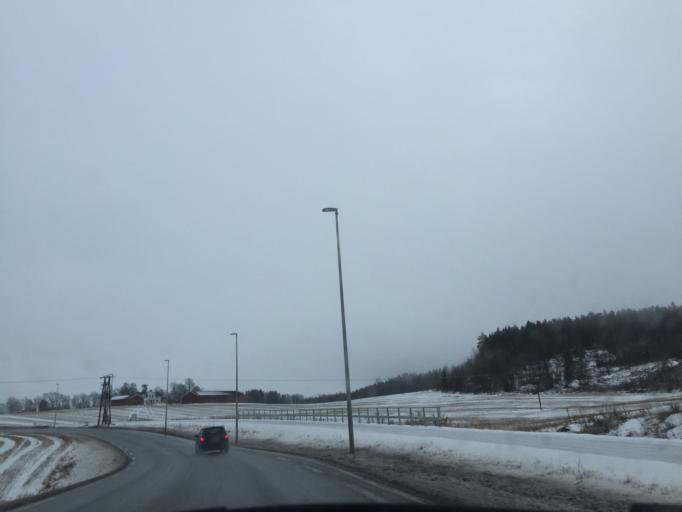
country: NO
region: Akershus
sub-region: Frogn
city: Drobak
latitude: 59.6609
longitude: 10.6662
